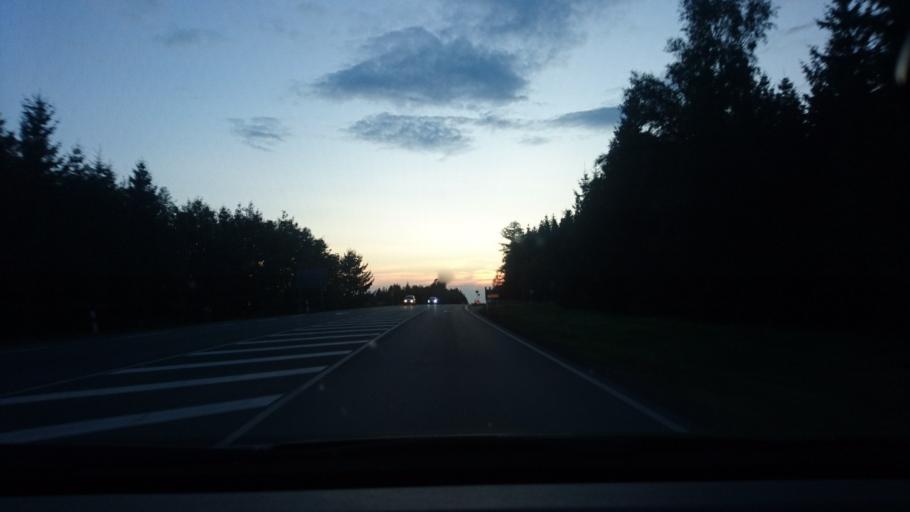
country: DE
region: Bavaria
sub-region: Upper Franconia
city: Leupoldsgrun
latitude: 50.3369
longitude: 11.7943
